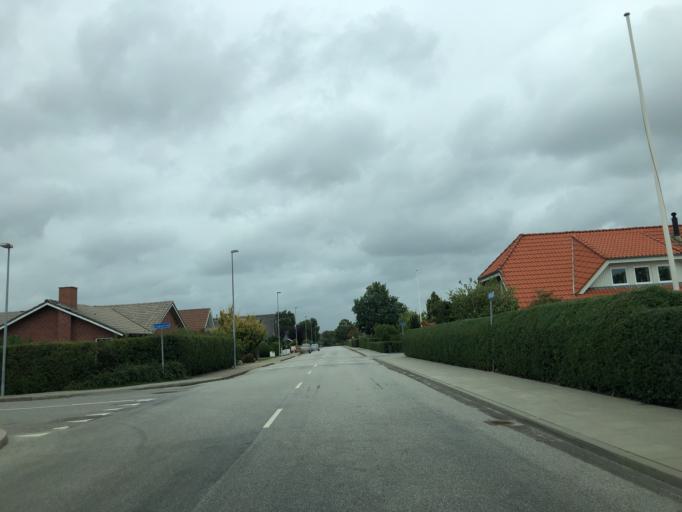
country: DK
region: Central Jutland
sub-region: Herning Kommune
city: Snejbjerg
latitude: 56.1278
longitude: 8.8975
